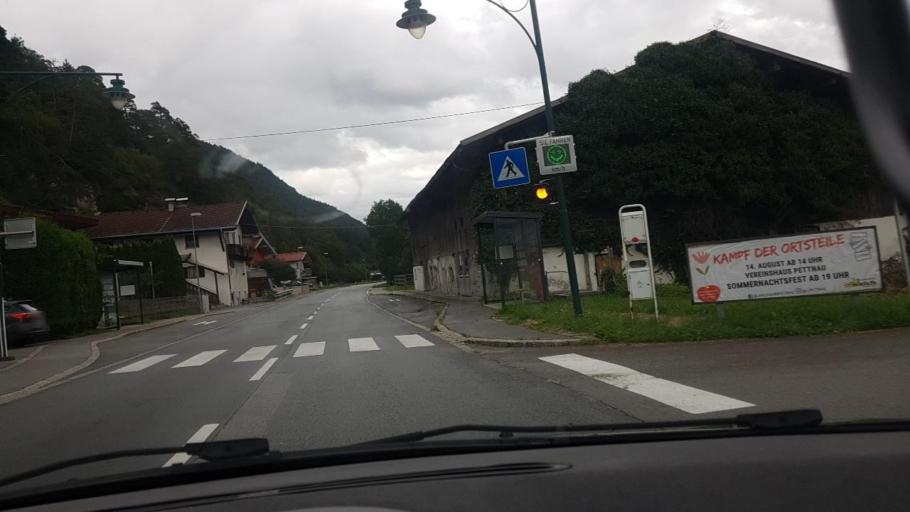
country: AT
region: Tyrol
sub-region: Politischer Bezirk Innsbruck Land
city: Pettnau
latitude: 47.3021
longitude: 11.1333
